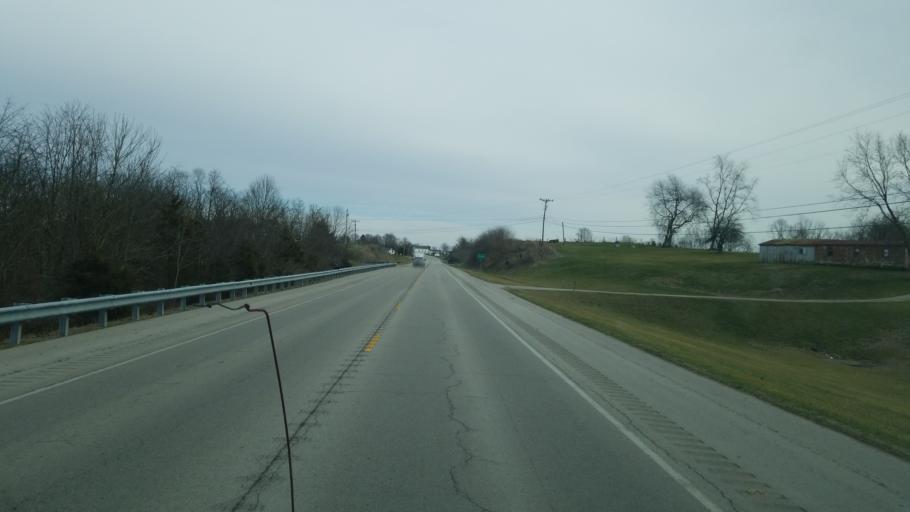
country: US
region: Kentucky
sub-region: Robertson County
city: Mount Olivet
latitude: 38.4586
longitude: -83.9401
